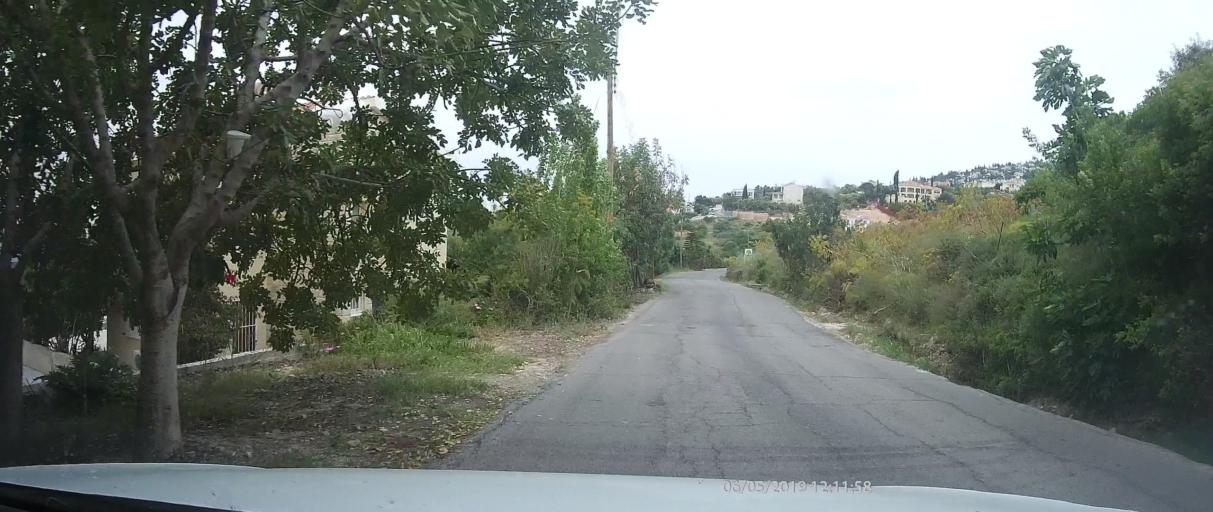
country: CY
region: Pafos
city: Tala
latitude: 34.8393
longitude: 32.4288
